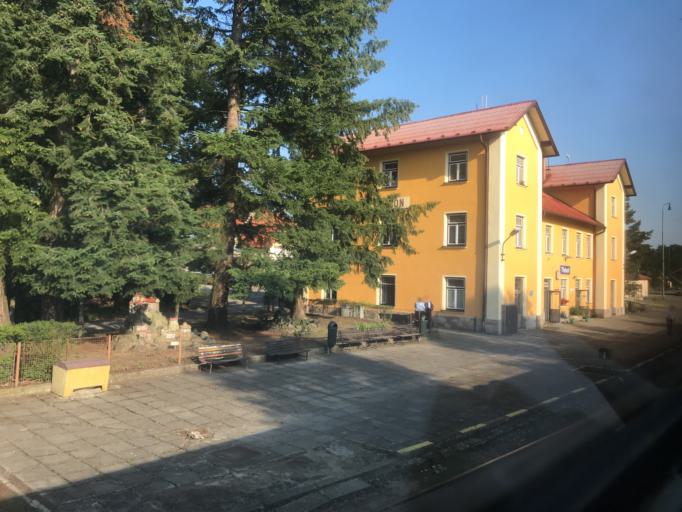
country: CZ
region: Jihocesky
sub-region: Okres Jindrichuv Hradec
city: Trebon
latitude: 49.0149
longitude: 14.7608
